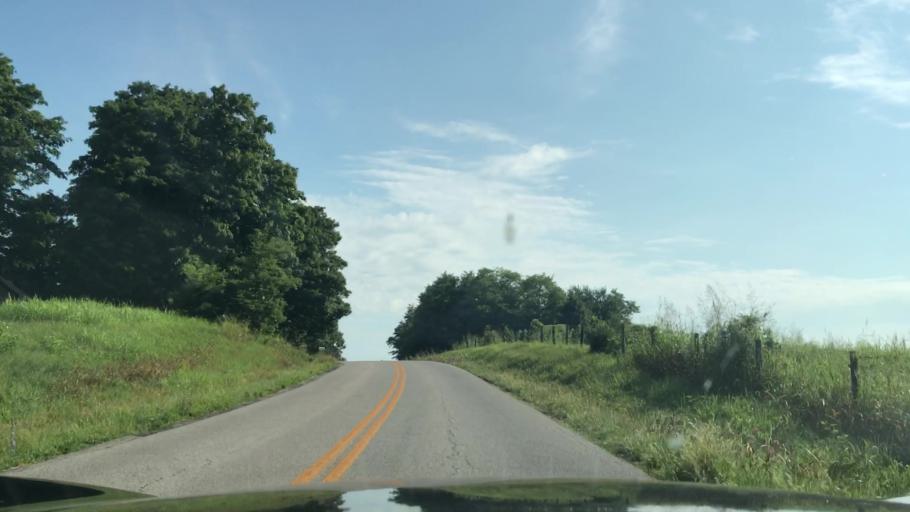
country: US
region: Kentucky
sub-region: Hart County
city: Munfordville
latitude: 37.2018
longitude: -85.7464
